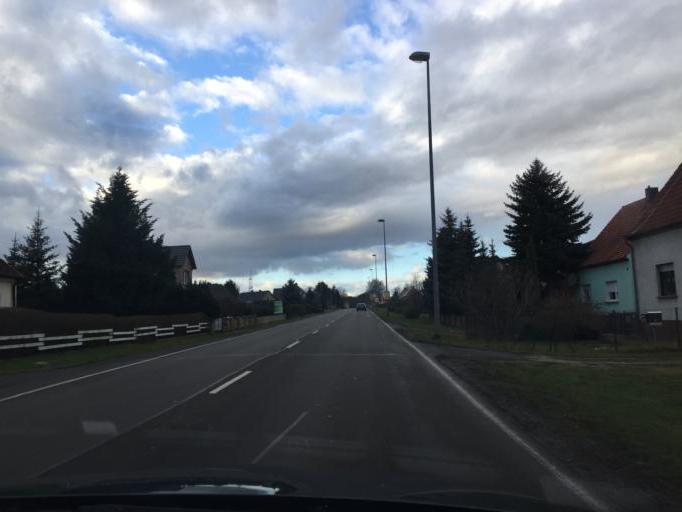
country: DE
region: Brandenburg
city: Kolkwitz
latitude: 51.7530
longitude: 14.1925
